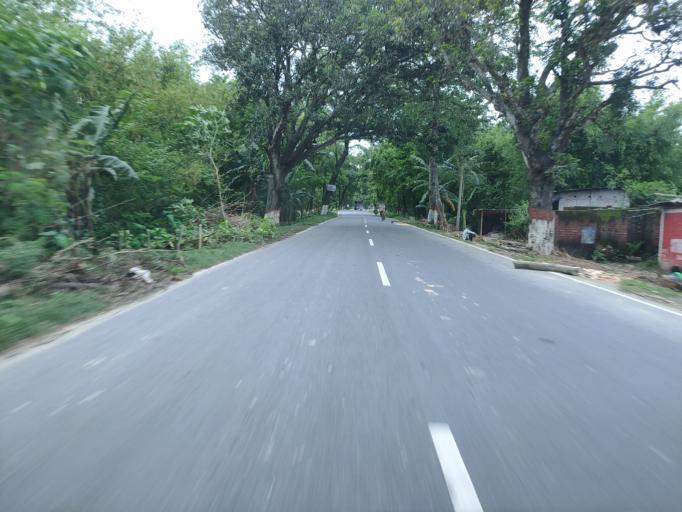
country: IN
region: West Bengal
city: Kishanganj
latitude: 26.1717
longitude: 87.9120
